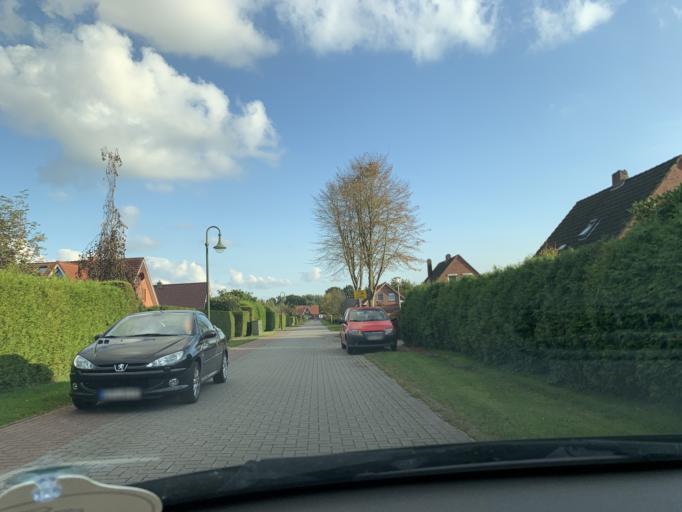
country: DE
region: Lower Saxony
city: Apen
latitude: 53.2434
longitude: 7.7850
